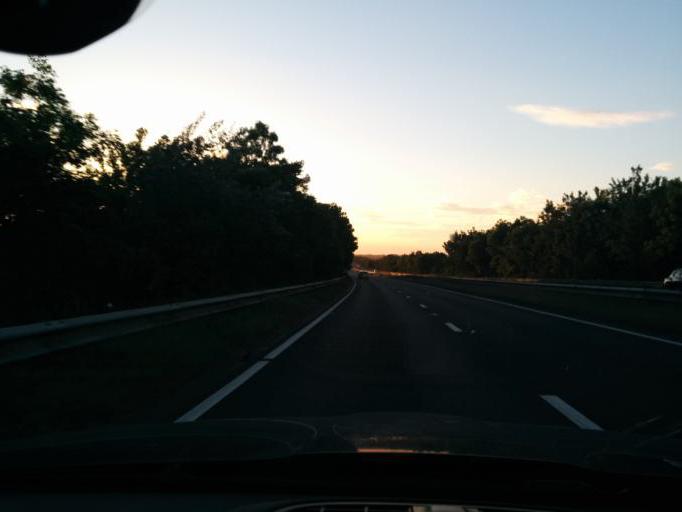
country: GB
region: England
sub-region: Northumberland
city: Seghill
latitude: 55.0503
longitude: -1.5550
